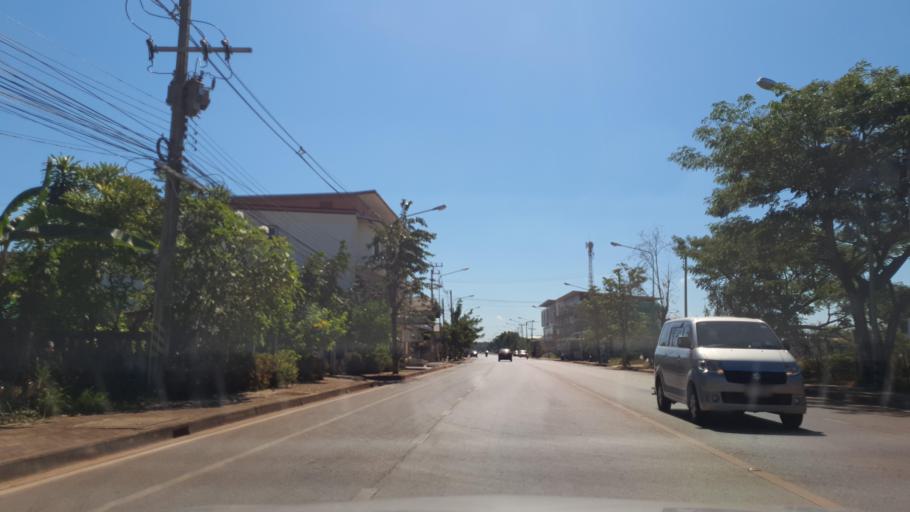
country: TH
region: Sakon Nakhon
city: Sakon Nakhon
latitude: 17.1557
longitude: 104.1267
